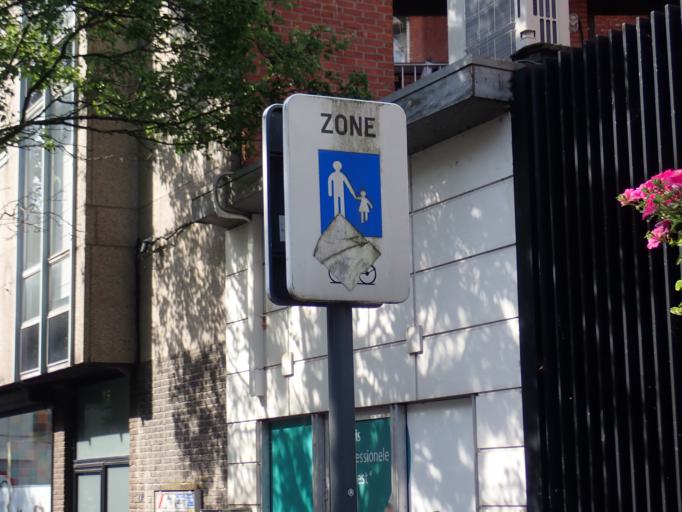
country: BE
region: Flanders
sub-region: Provincie Antwerpen
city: Turnhout
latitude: 51.3227
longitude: 4.9448
